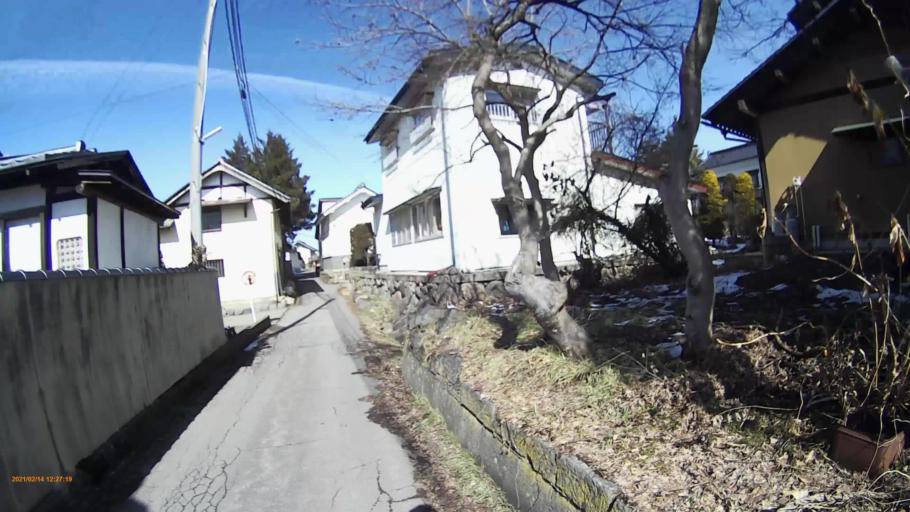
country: JP
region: Nagano
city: Nakano
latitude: 36.7508
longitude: 138.3556
